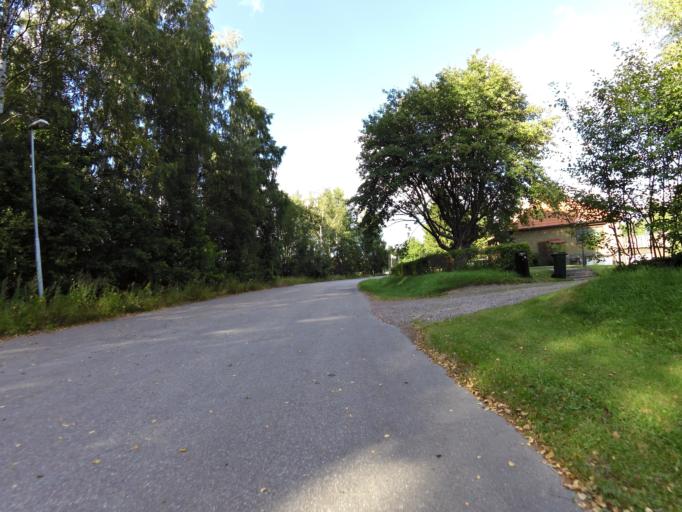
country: SE
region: Gaevleborg
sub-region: Gavle Kommun
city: Gavle
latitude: 60.6933
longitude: 17.1555
